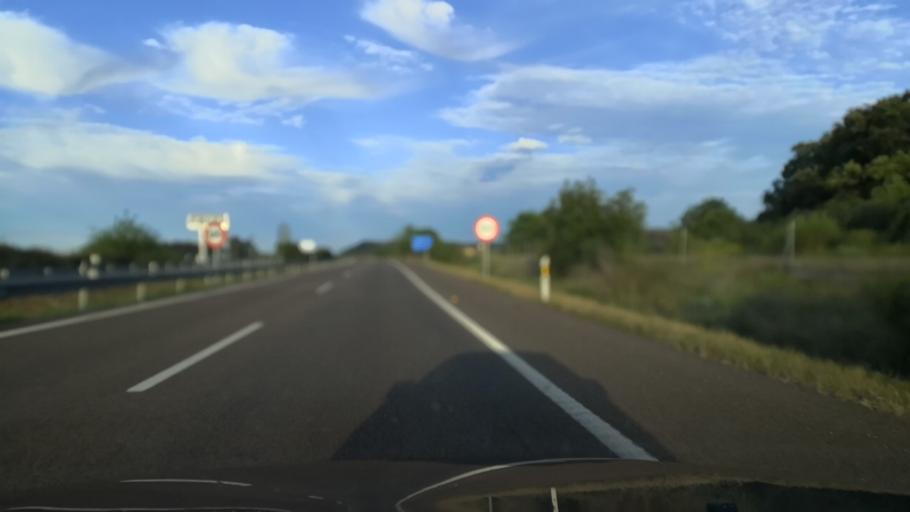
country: ES
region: Extremadura
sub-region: Provincia de Badajoz
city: Lobon
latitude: 38.8564
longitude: -6.6004
